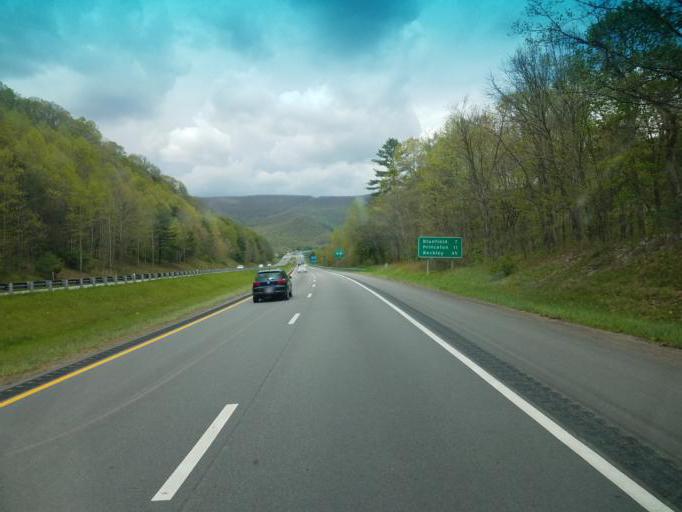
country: US
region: West Virginia
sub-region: Mercer County
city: Bluefield
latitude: 37.2474
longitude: -81.1141
